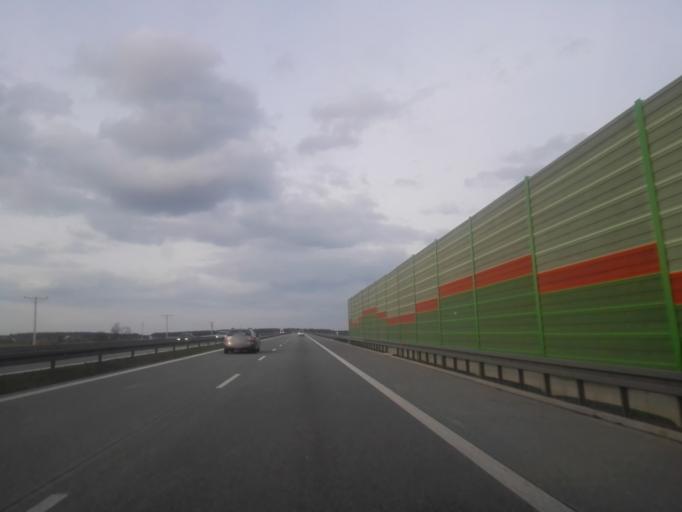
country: PL
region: Lodz Voivodeship
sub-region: Powiat tomaszowski
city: Lubochnia
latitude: 51.6149
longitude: 20.0801
